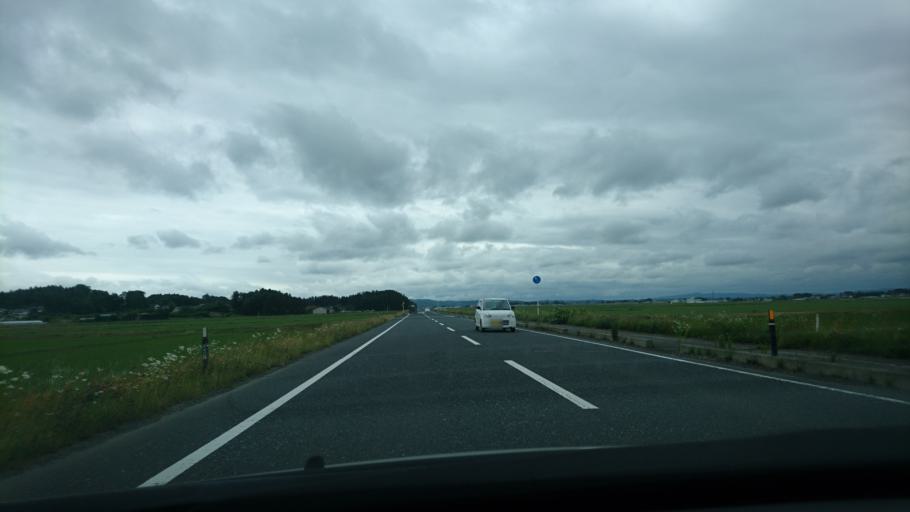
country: JP
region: Miyagi
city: Wakuya
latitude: 38.7023
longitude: 141.2602
